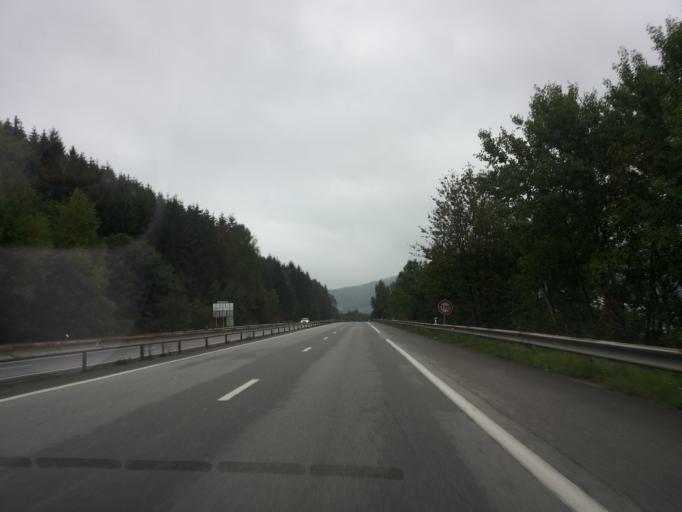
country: FR
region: Lorraine
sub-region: Departement des Vosges
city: Eloyes
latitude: 48.0818
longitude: 6.5956
